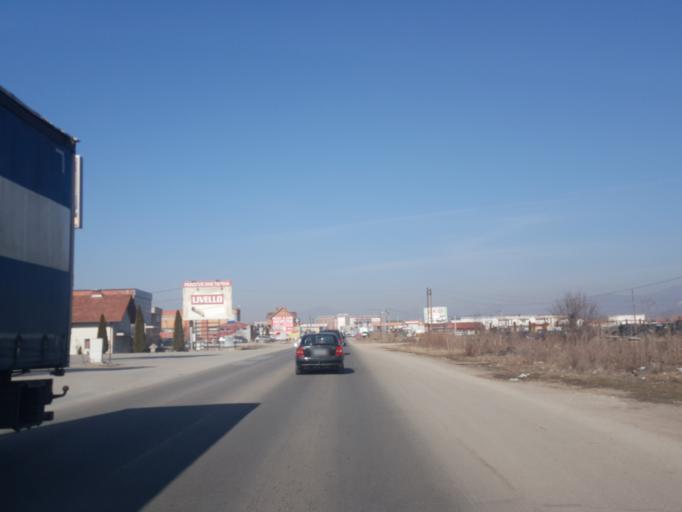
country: XK
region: Mitrovica
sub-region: Vushtrri
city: Vushtrri
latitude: 42.8112
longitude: 20.9862
